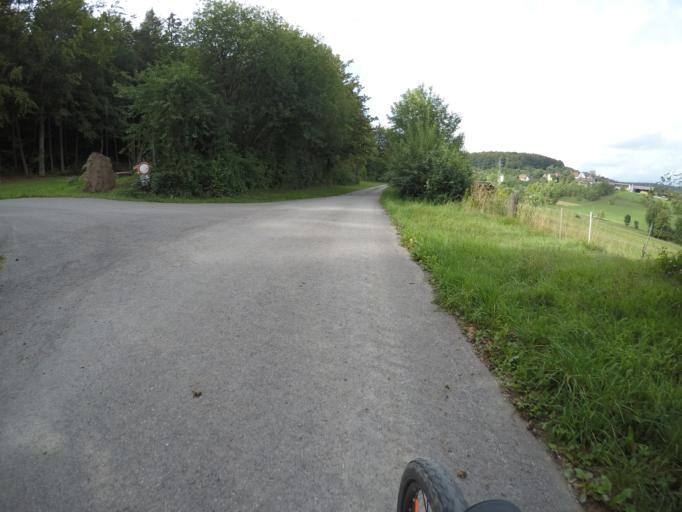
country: DE
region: Baden-Wuerttemberg
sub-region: Karlsruhe Region
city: Simmozheim
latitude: 48.7416
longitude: 8.8204
